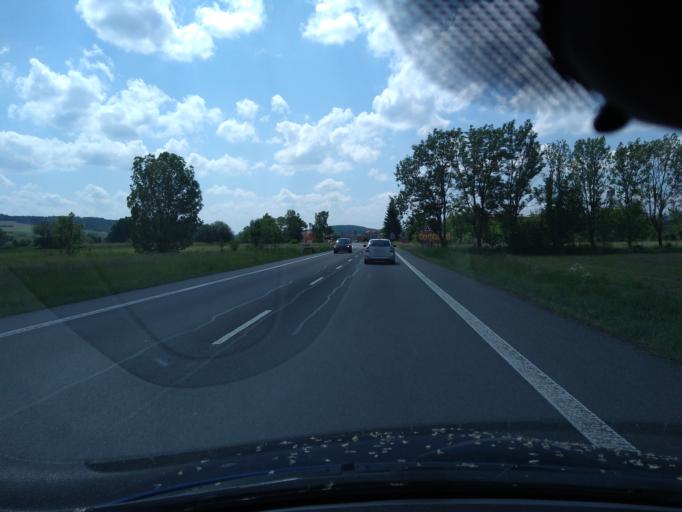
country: CZ
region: Plzensky
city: Svihov
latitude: 49.4882
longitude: 13.2869
